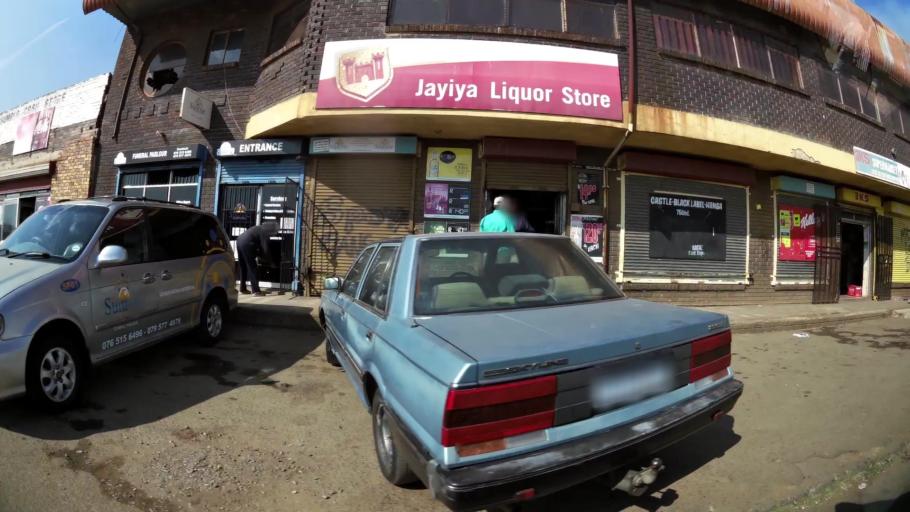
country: ZA
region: Gauteng
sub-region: Ekurhuleni Metropolitan Municipality
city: Benoni
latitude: -26.1461
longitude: 28.4096
